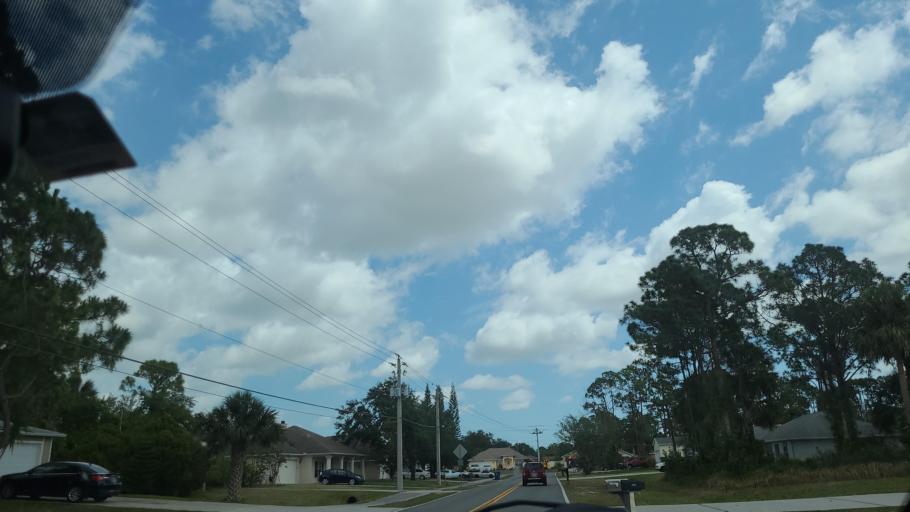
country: US
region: Florida
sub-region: Brevard County
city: West Melbourne
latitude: 28.0088
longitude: -80.6627
